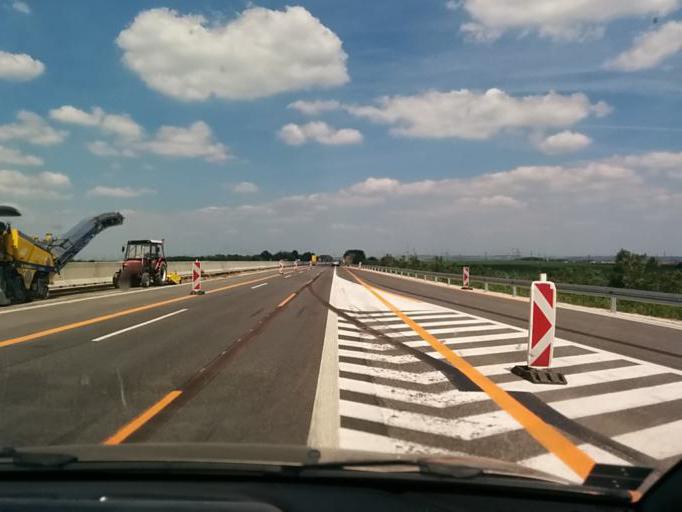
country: SK
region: Trnavsky
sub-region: Okres Trnava
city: Trnava
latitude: 48.3397
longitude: 17.6342
